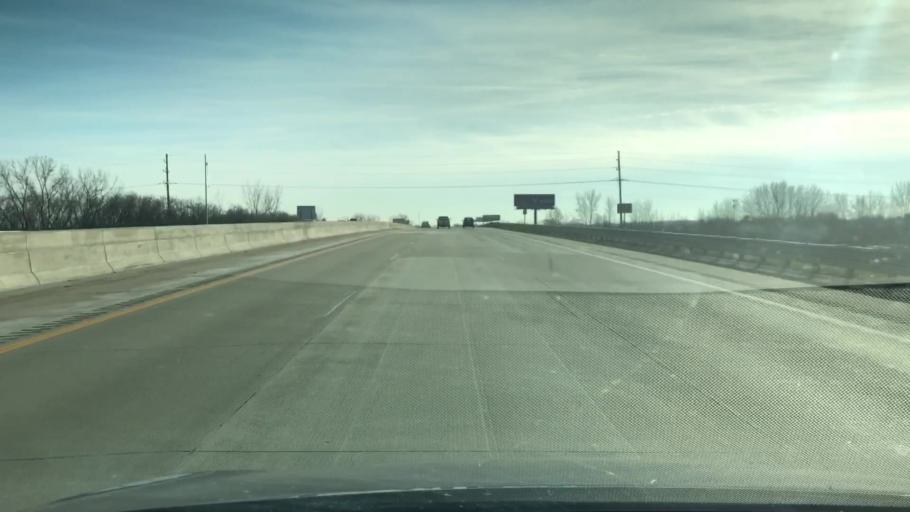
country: US
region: Michigan
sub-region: Saginaw County
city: Buena Vista
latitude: 43.4448
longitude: -83.8910
